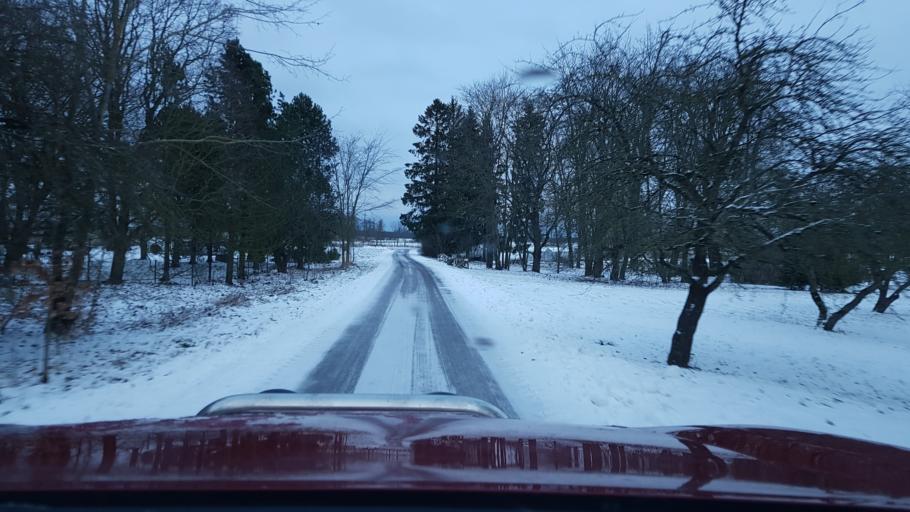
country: EE
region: Harju
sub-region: Maardu linn
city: Maardu
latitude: 59.4277
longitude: 25.0203
